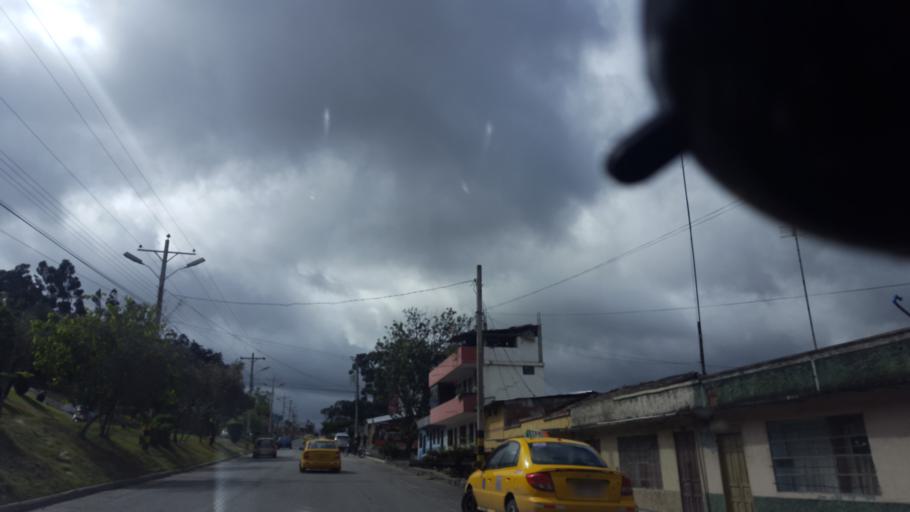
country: EC
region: Loja
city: Loja
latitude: -3.9994
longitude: -79.2078
